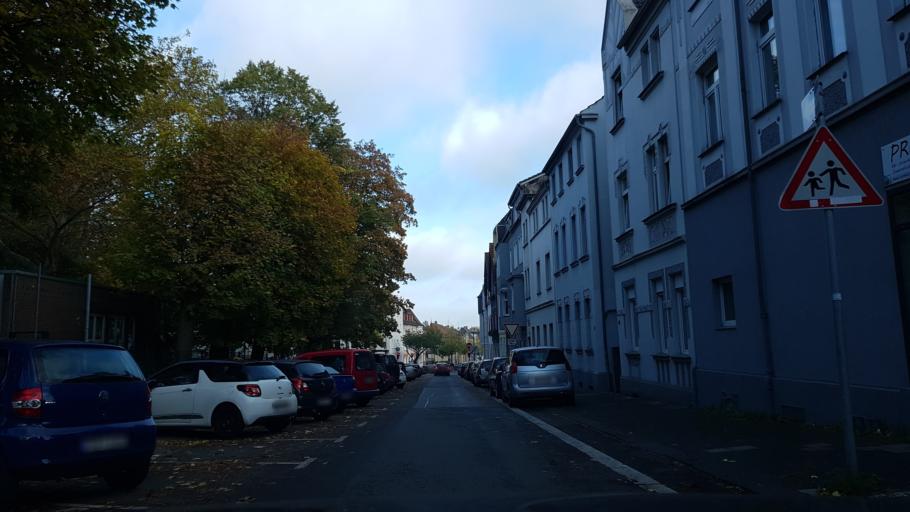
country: DE
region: North Rhine-Westphalia
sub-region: Regierungsbezirk Dusseldorf
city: Muelheim (Ruhr)
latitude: 51.4217
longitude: 6.8551
